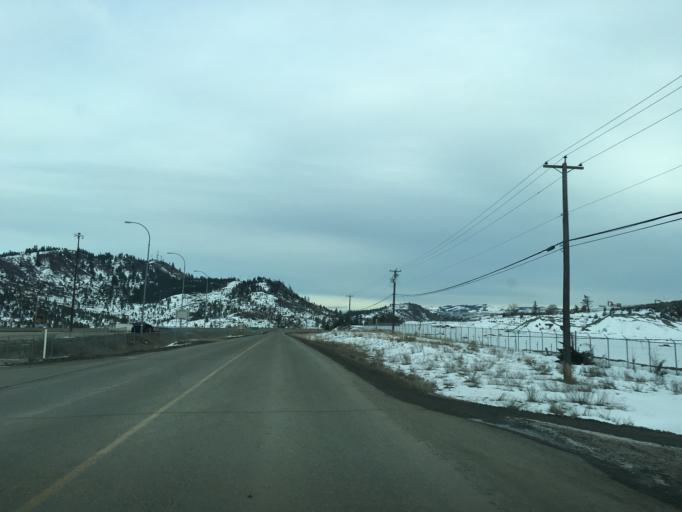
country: CA
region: British Columbia
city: Kamloops
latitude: 50.6649
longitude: -120.4241
